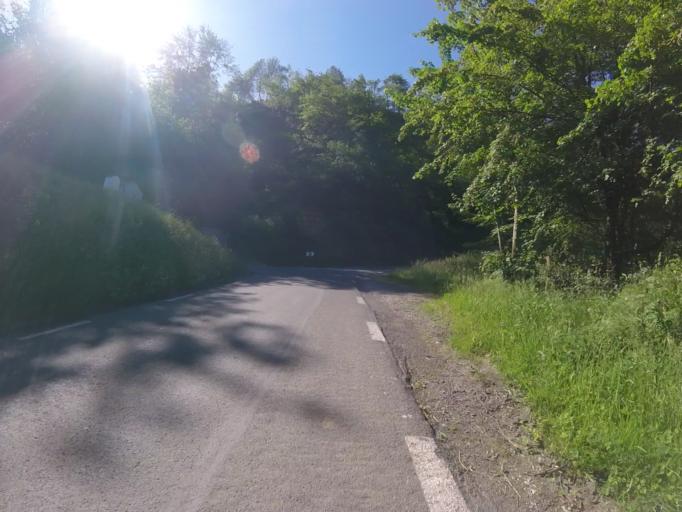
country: ES
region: Basque Country
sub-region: Provincia de Guipuzcoa
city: Beizama
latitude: 43.1316
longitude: -2.1950
